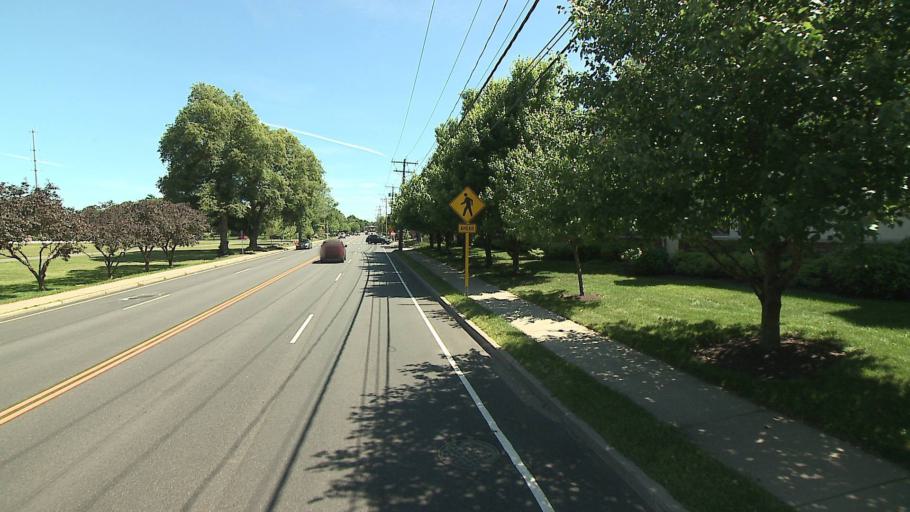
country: US
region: Connecticut
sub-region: Fairfield County
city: Darien
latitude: 41.0670
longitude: -73.4790
